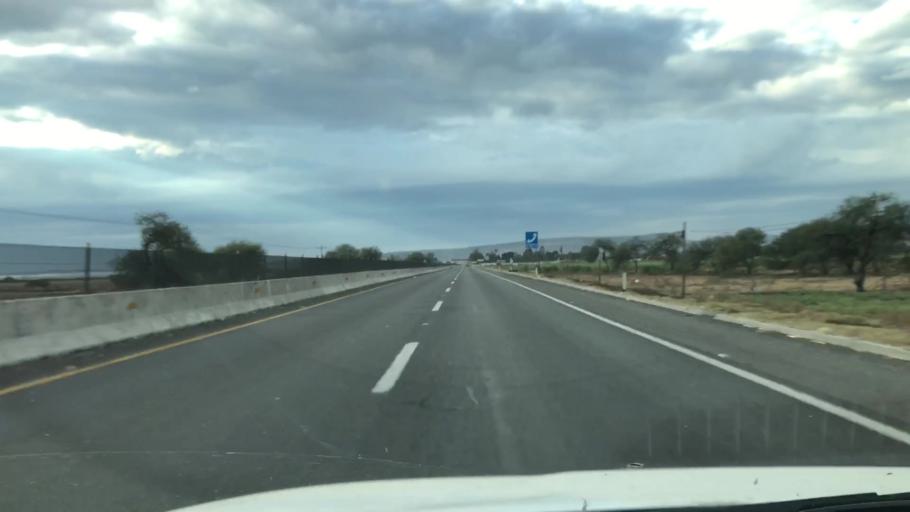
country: MX
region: Guanajuato
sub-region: Penjamo
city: Estacion la Piedad
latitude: 20.3859
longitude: -101.9110
